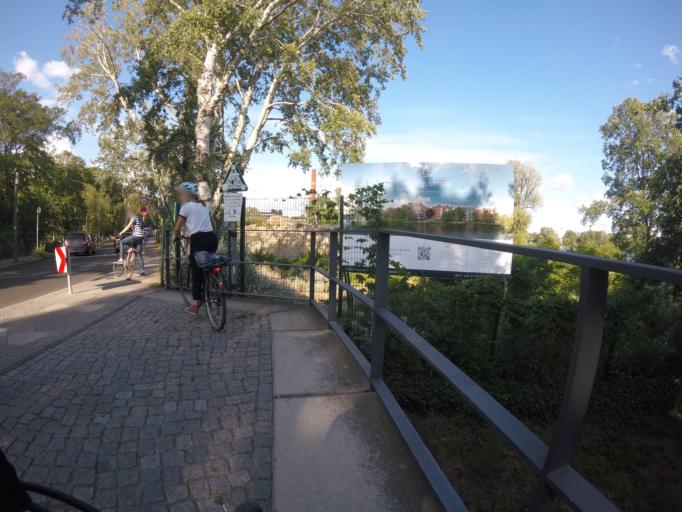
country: DE
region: Berlin
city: Hakenfelde
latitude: 52.5469
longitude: 13.2163
